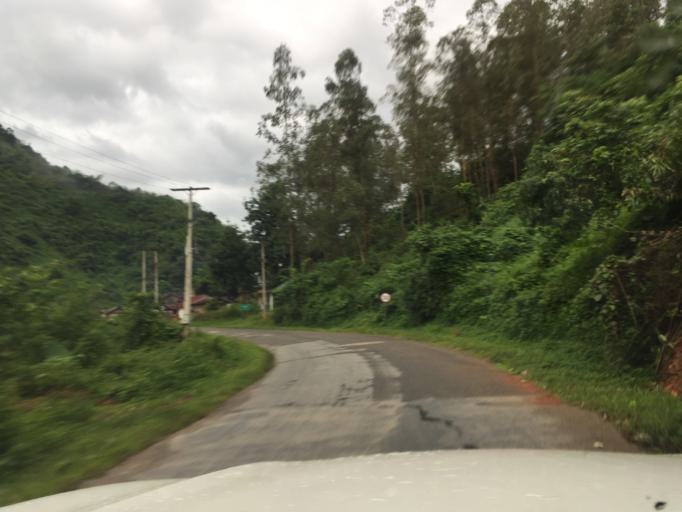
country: LA
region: Oudomxai
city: Muang La
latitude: 20.9883
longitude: 102.2274
